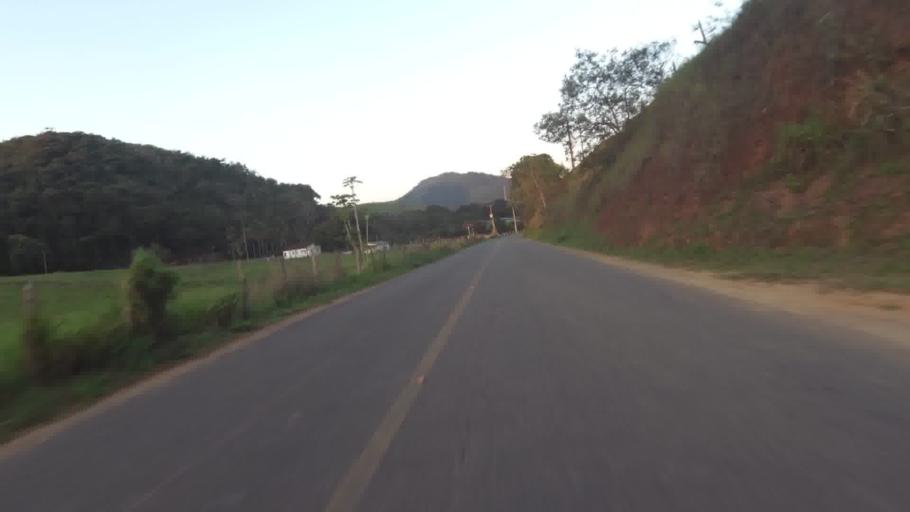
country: BR
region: Espirito Santo
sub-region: Alfredo Chaves
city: Alfredo Chaves
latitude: -20.6506
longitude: -40.6492
